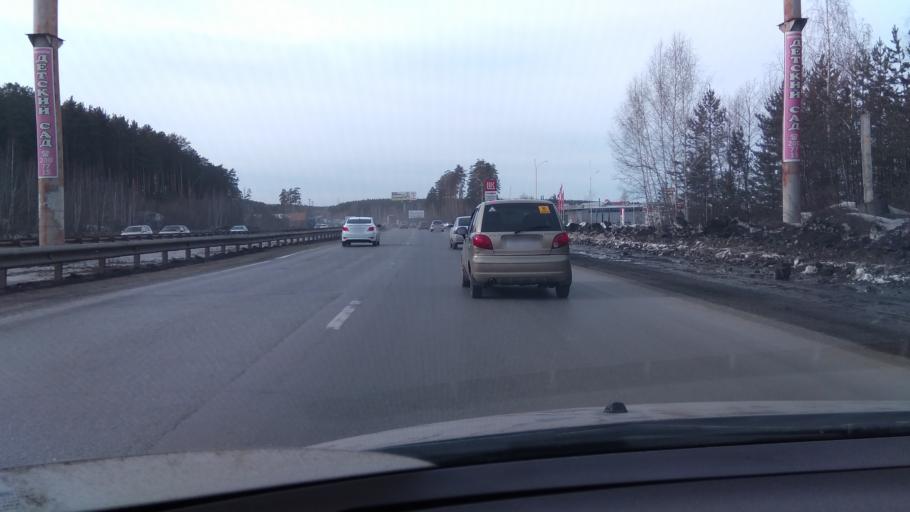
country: RU
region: Sverdlovsk
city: Shirokaya Rechka
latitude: 56.8178
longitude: 60.5092
